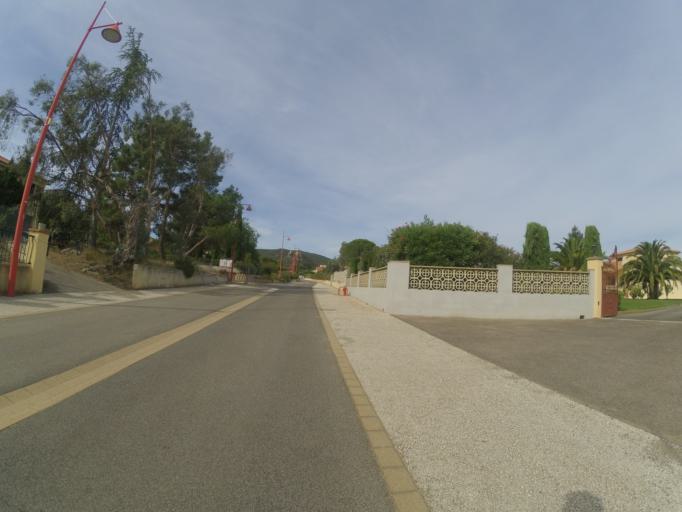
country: FR
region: Languedoc-Roussillon
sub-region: Departement des Pyrenees-Orientales
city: Millas
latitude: 42.6567
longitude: 2.6711
